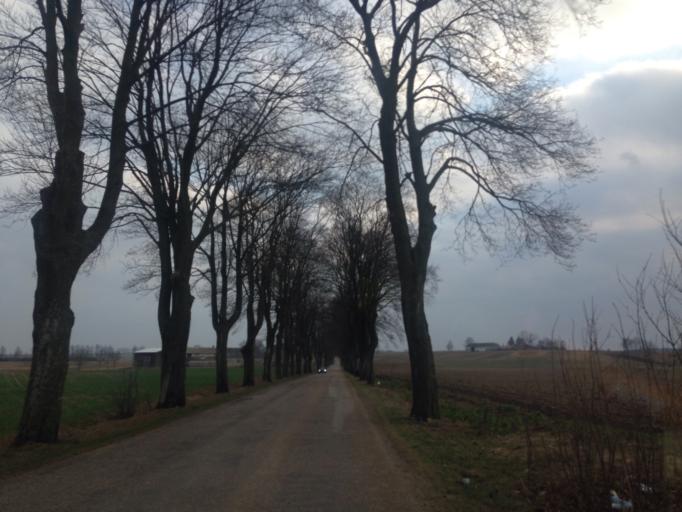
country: PL
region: Kujawsko-Pomorskie
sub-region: Powiat brodnicki
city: Brzozie
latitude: 53.3430
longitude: 19.7131
